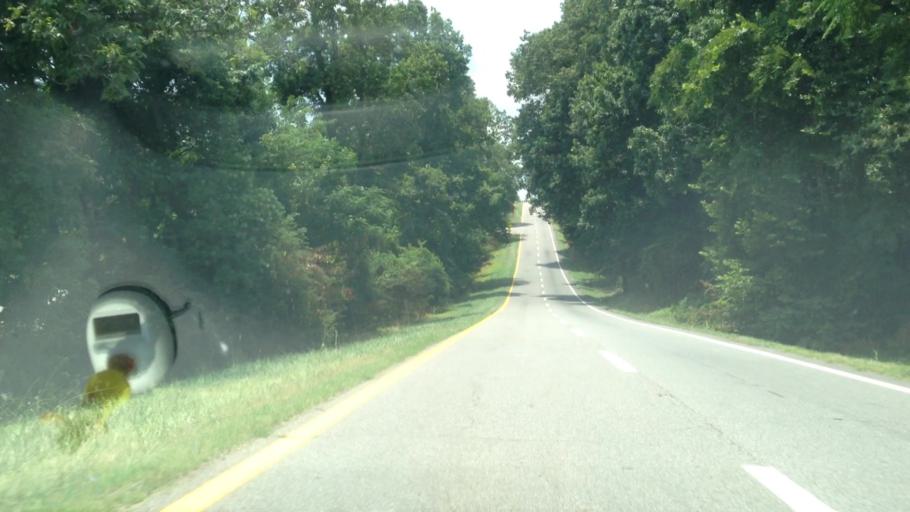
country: US
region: Virginia
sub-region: Henry County
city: Horse Pasture
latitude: 36.5643
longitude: -79.8782
